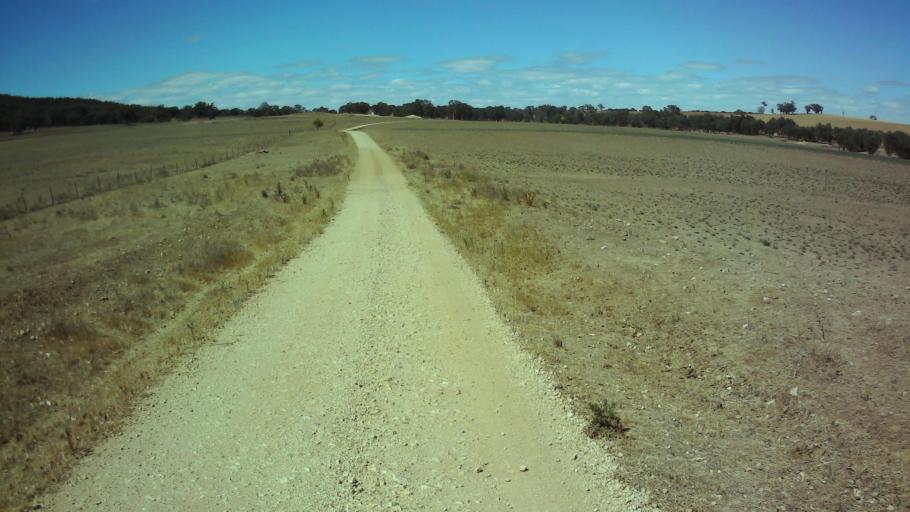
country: AU
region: New South Wales
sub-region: Weddin
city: Grenfell
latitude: -34.0387
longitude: 148.4322
